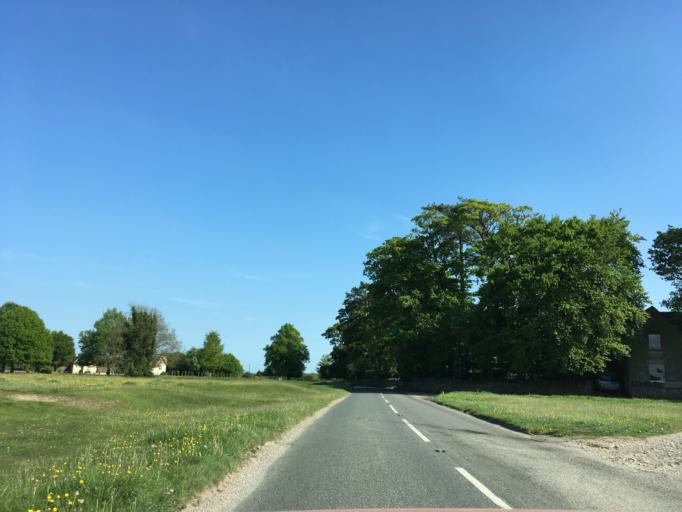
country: GB
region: England
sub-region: Gloucestershire
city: Minchinhampton
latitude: 51.7088
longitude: -2.2038
